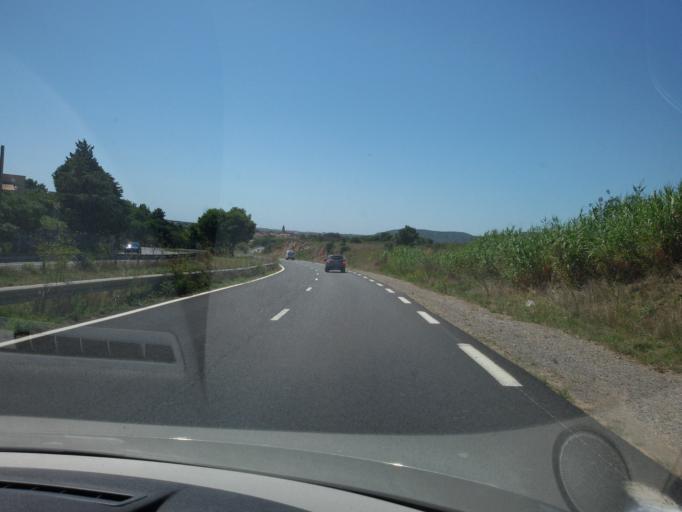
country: FR
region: Languedoc-Roussillon
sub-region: Departement de l'Herault
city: Mireval
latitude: 43.5198
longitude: 3.8092
